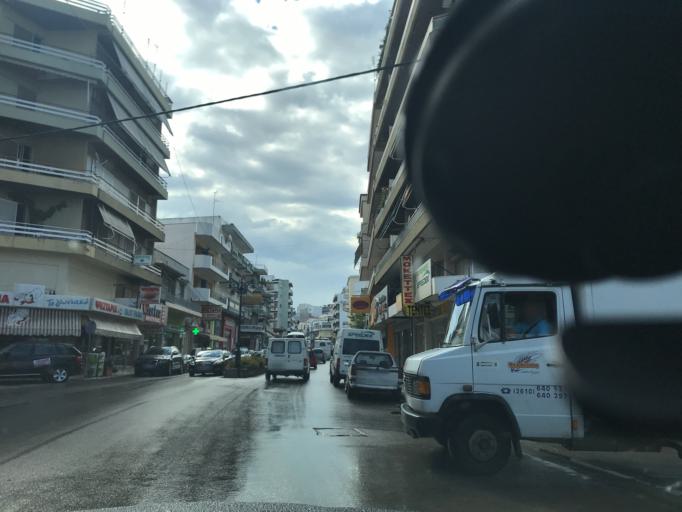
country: GR
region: West Greece
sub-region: Nomos Ileias
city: Pyrgos
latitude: 37.6748
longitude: 21.4349
